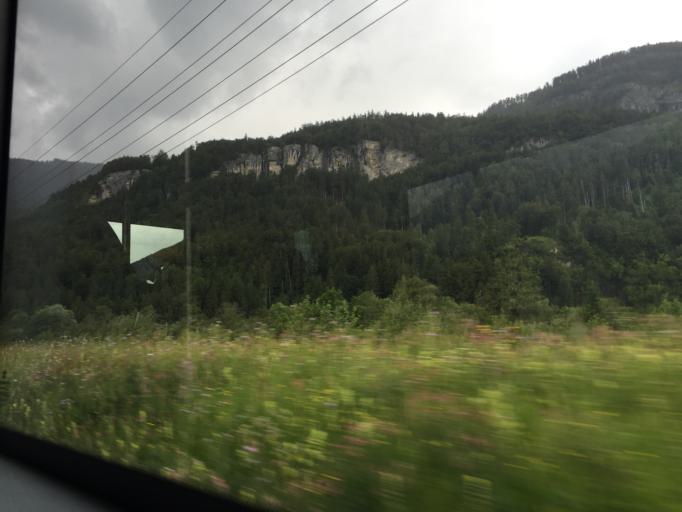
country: CH
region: Bern
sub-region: Interlaken-Oberhasli District
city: Meiringen
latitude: 46.7420
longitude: 8.1445
